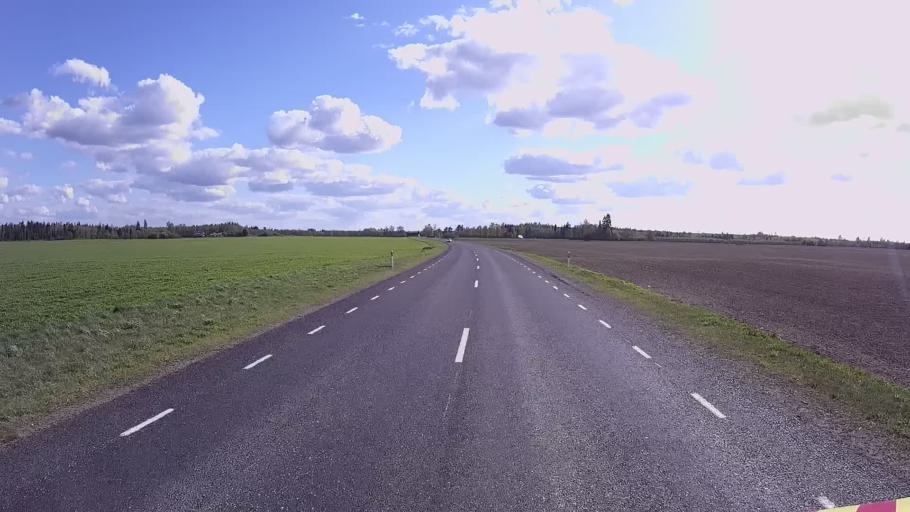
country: EE
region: Jogevamaa
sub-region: Jogeva linn
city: Jogeva
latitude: 58.7254
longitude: 26.1923
